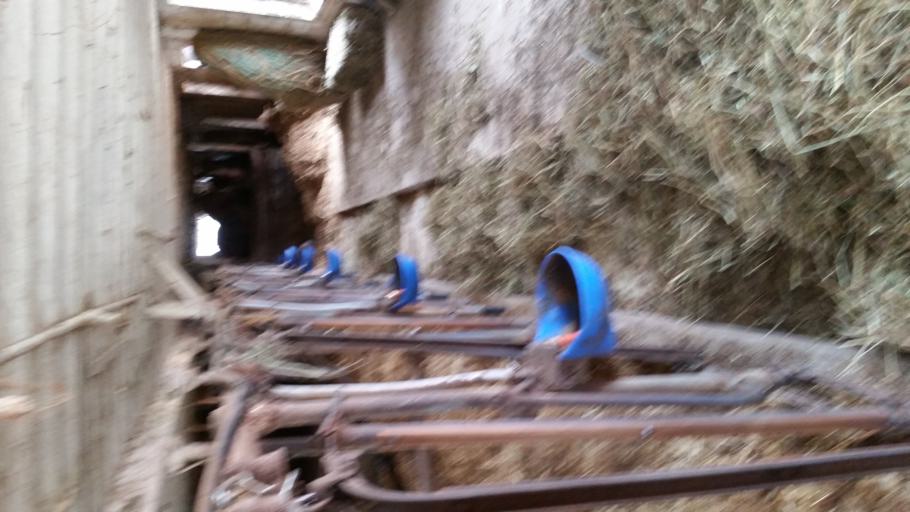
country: US
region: Wisconsin
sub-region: Clark County
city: Neillsville
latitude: 44.5856
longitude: -90.4728
